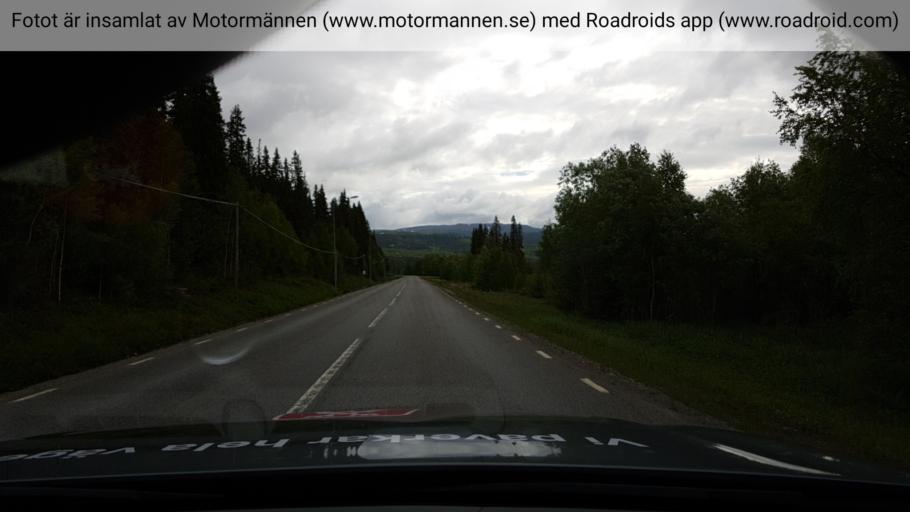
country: NO
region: Nord-Trondelag
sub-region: Lierne
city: Sandvika
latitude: 64.4803
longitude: 14.1200
